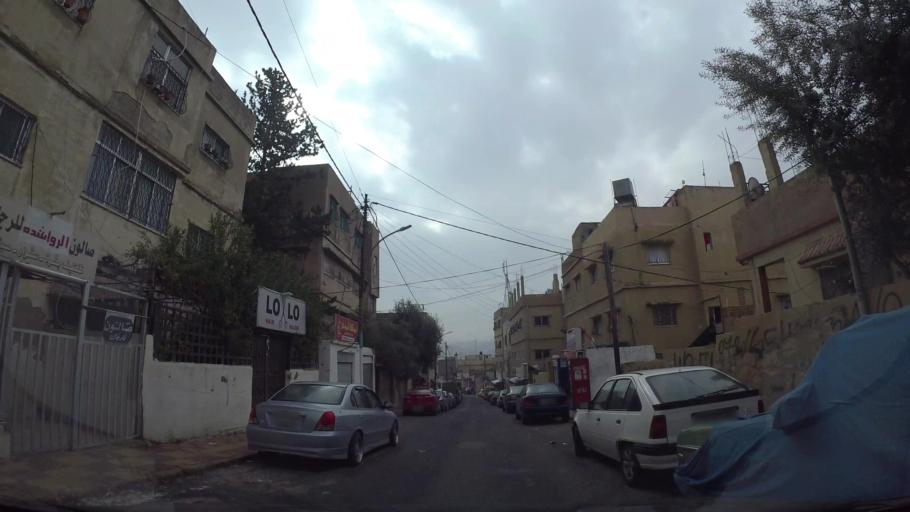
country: JO
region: Amman
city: Amman
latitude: 31.9588
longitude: 35.9382
